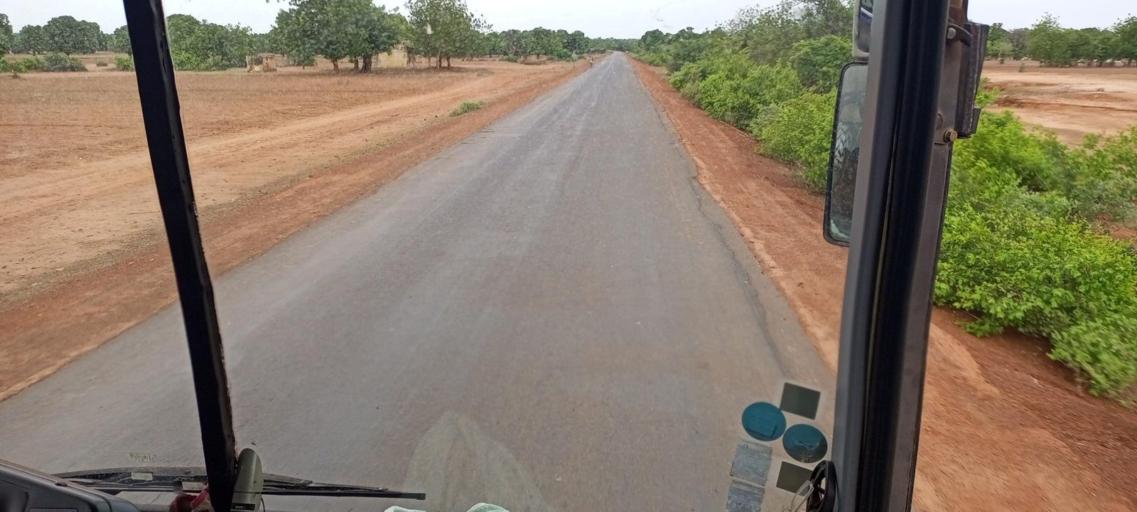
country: ML
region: Segou
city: Bla
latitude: 12.6849
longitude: -5.7236
